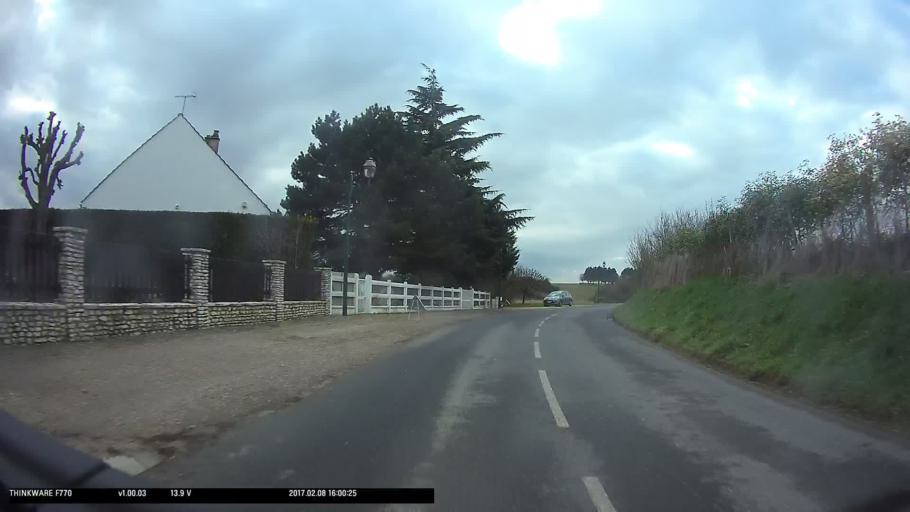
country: FR
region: Ile-de-France
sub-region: Departement du Val-d'Oise
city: Us
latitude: 49.0993
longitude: 1.9647
